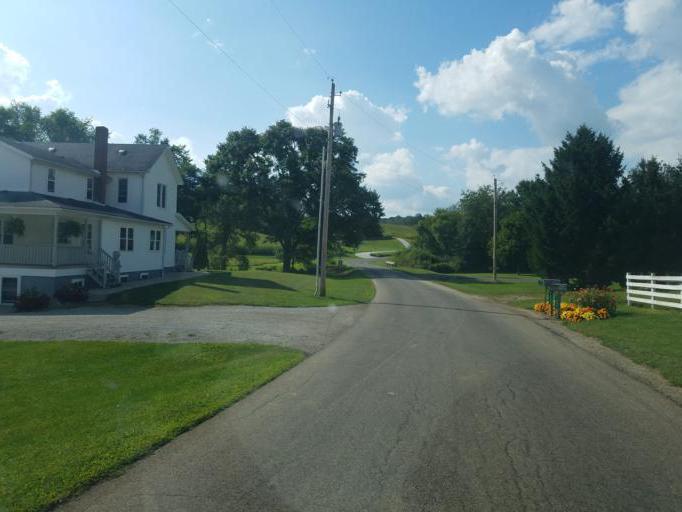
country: US
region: Ohio
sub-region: Knox County
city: Danville
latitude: 40.4697
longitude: -82.2967
